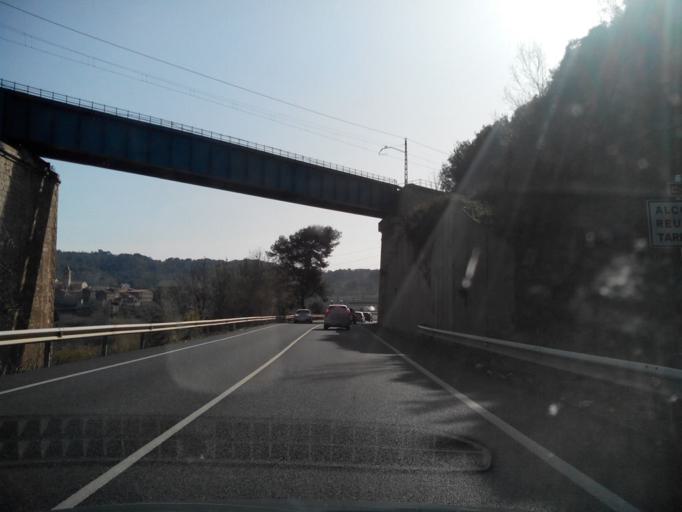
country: ES
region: Catalonia
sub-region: Provincia de Tarragona
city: Alcover
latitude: 41.3042
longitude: 1.1945
